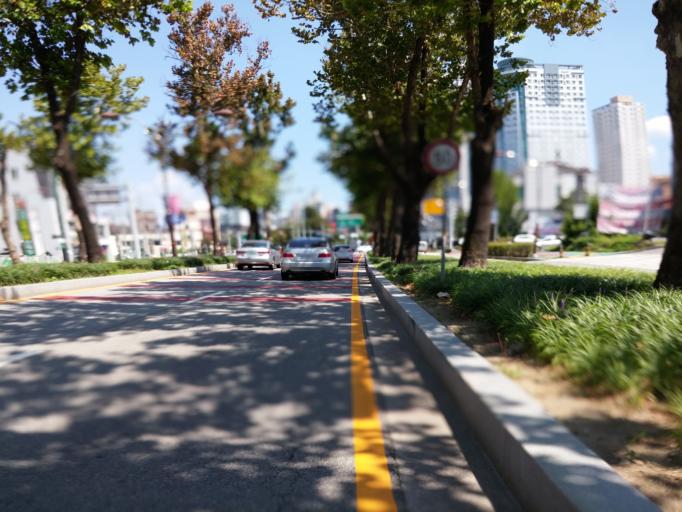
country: KR
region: Chungcheongbuk-do
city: Cheongju-si
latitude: 36.6268
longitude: 127.4245
